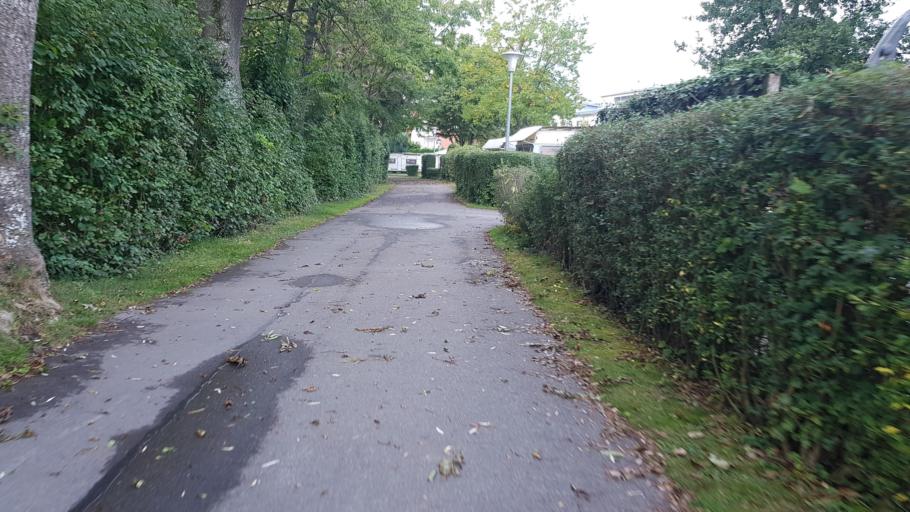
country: DE
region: Baden-Wuerttemberg
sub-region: Tuebingen Region
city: Immenstaad am Bodensee
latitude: 47.6658
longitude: 9.3754
